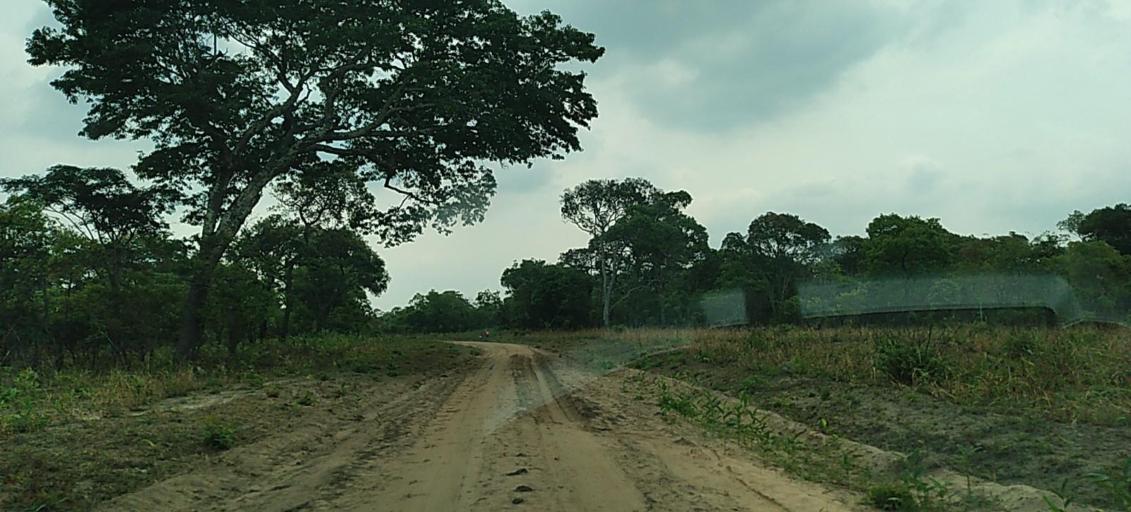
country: ZM
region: North-Western
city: Mwinilunga
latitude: -11.4147
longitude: 24.6089
